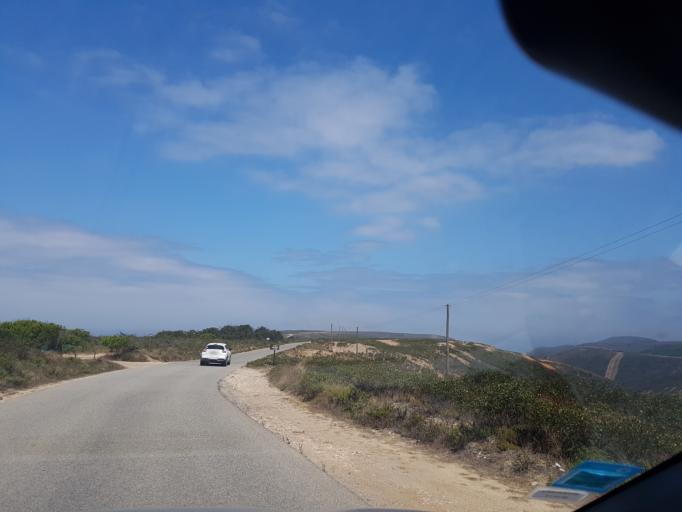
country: PT
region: Faro
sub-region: Vila do Bispo
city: Vila do Bispo
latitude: 37.0918
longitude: -8.9321
